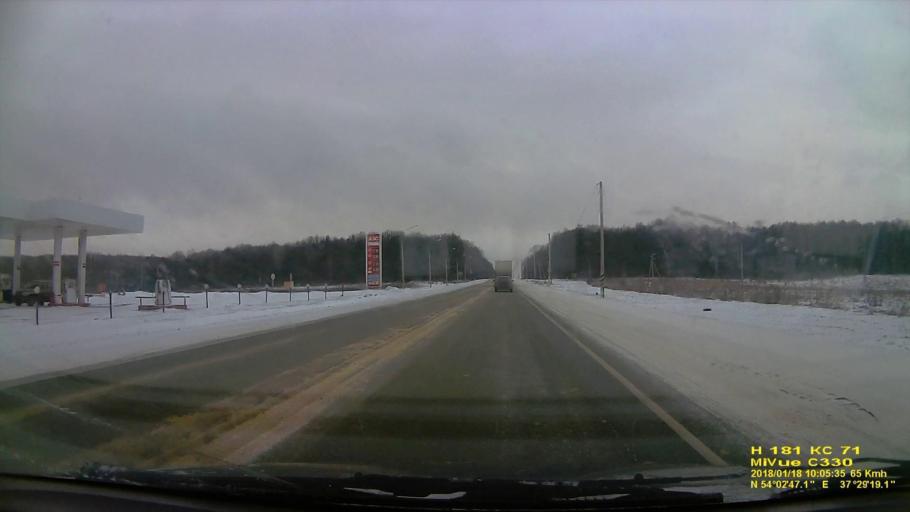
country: RU
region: Tula
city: Pervomayskiy
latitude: 54.0463
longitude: 37.4886
